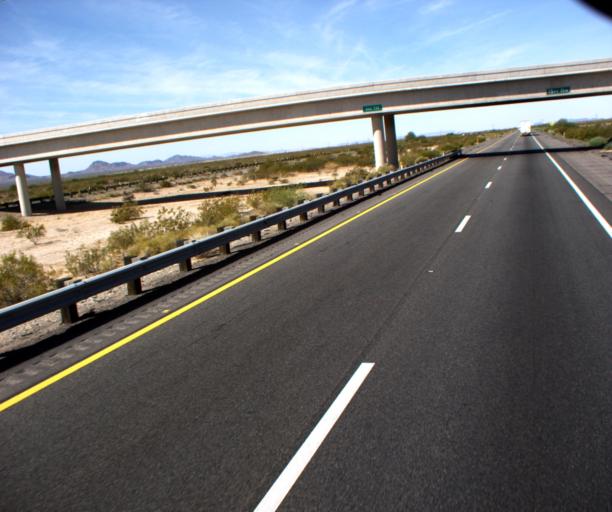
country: US
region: Arizona
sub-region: La Paz County
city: Salome
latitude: 33.5691
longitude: -113.3517
